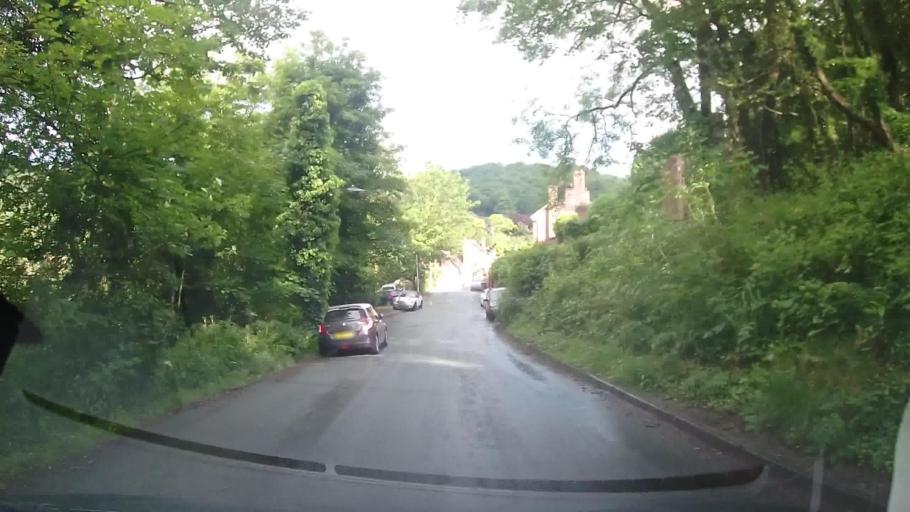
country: GB
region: England
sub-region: Telford and Wrekin
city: Ironbridge
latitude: 52.6425
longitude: -2.4959
